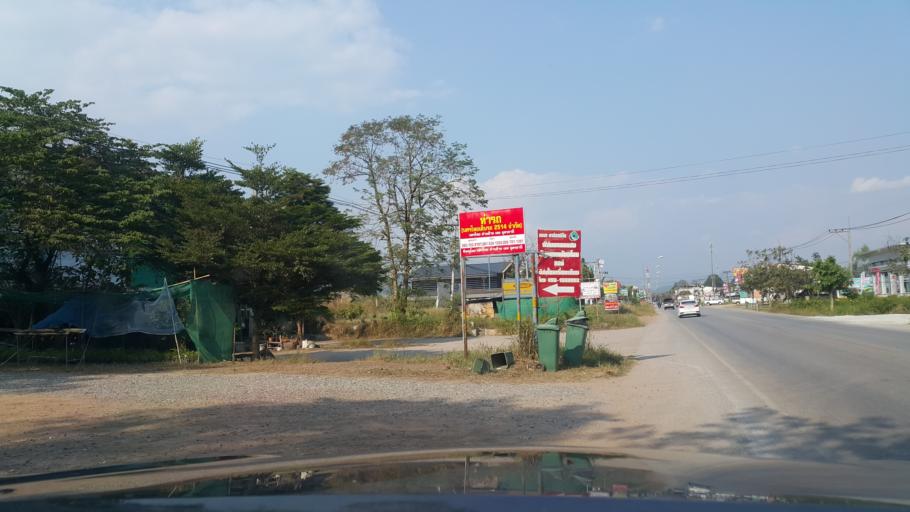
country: TH
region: Phitsanulok
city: Nakhon Thai
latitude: 17.1000
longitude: 100.8357
